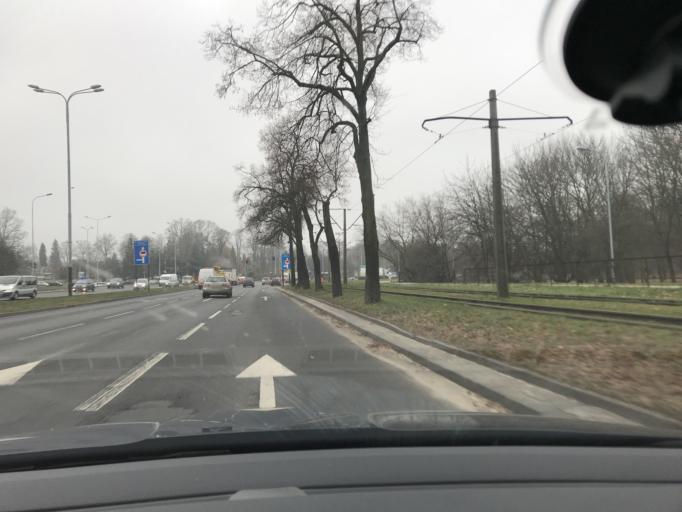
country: PL
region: Lodz Voivodeship
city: Lodz
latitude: 51.7941
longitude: 19.4882
